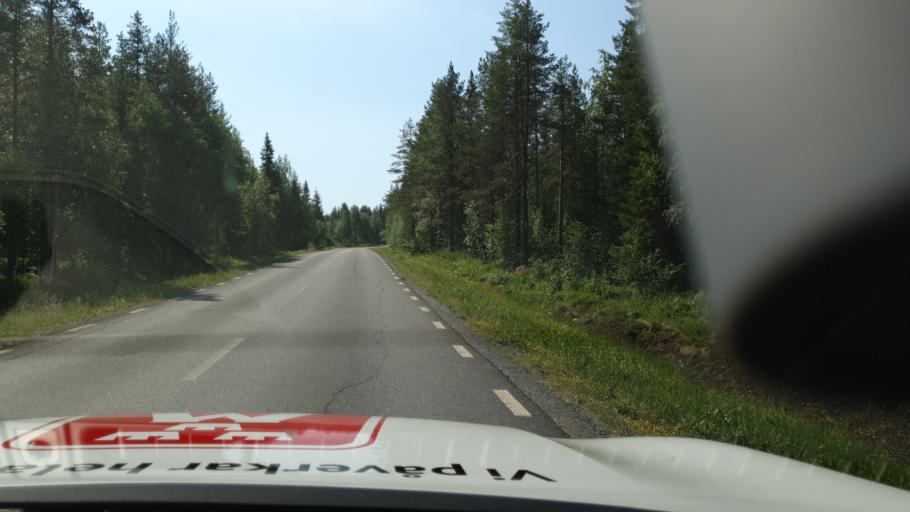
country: SE
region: Vaesterbotten
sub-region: Skelleftea Kommun
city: Langsele
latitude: 64.9958
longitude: 20.0901
